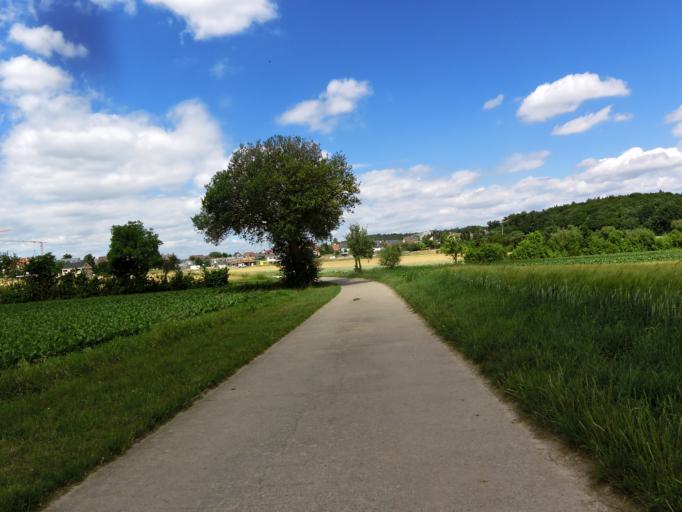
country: DE
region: Bavaria
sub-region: Regierungsbezirk Unterfranken
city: Kist
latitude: 49.7396
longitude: 9.8483
